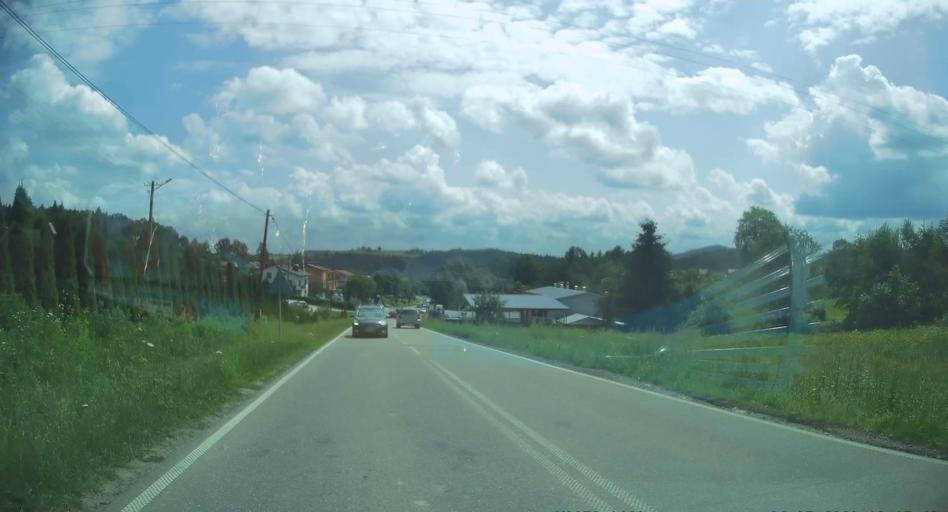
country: PL
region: Lesser Poland Voivodeship
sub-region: Powiat nowosadecki
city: Nowy Sacz
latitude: 49.6669
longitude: 20.7574
